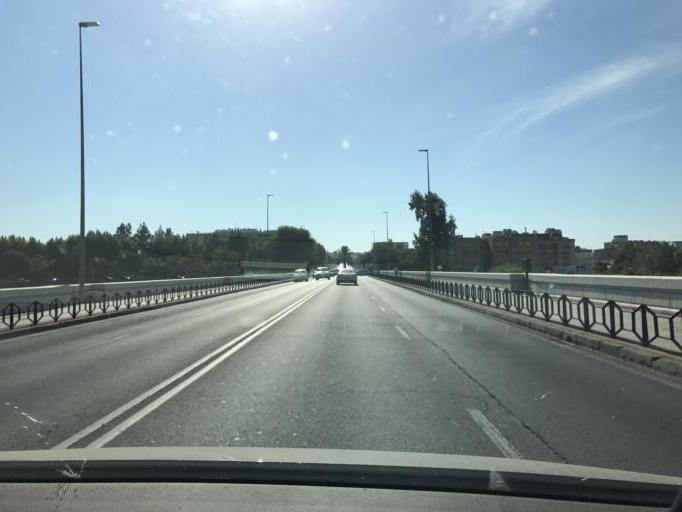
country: ES
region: Andalusia
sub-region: Province of Cordoba
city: Cordoba
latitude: 37.8721
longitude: -4.7829
